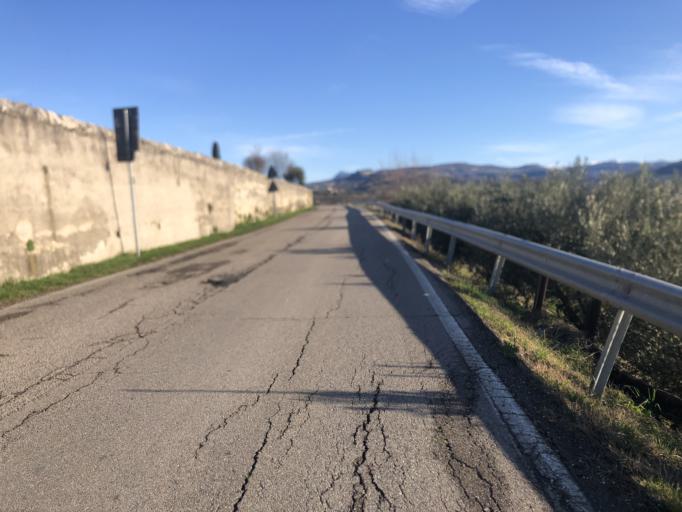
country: IT
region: Veneto
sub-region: Provincia di Verona
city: San Pietro in Cariano
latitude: 45.5116
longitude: 10.8883
